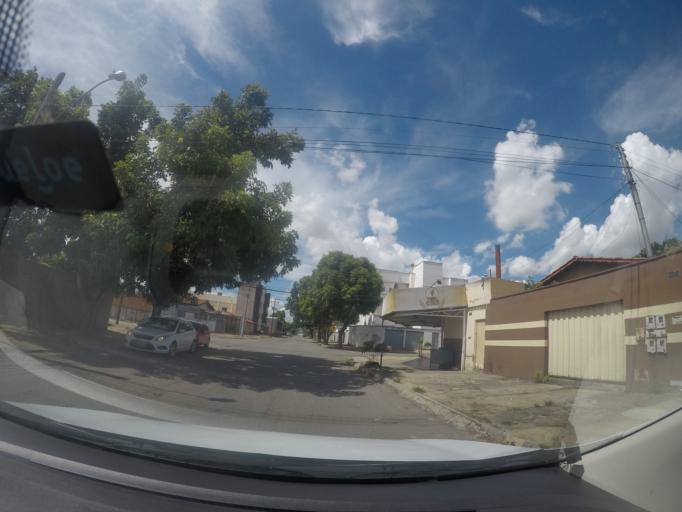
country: BR
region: Goias
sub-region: Goiania
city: Goiania
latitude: -16.6793
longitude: -49.3173
